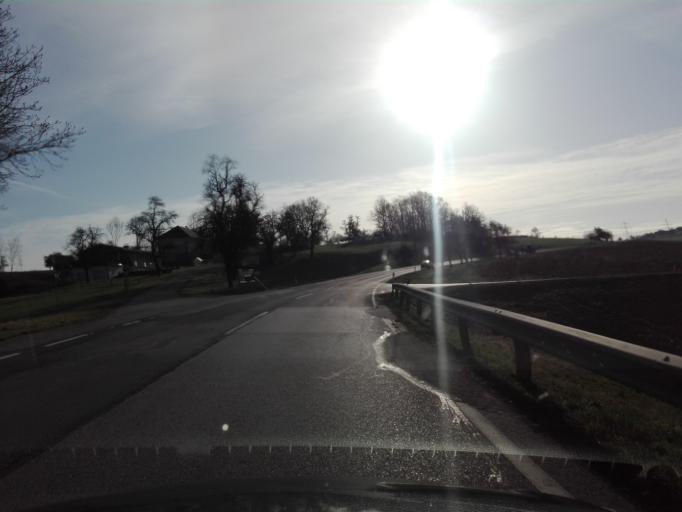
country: AT
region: Lower Austria
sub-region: Politischer Bezirk Amstetten
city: Strengberg
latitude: 48.1400
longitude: 14.6728
